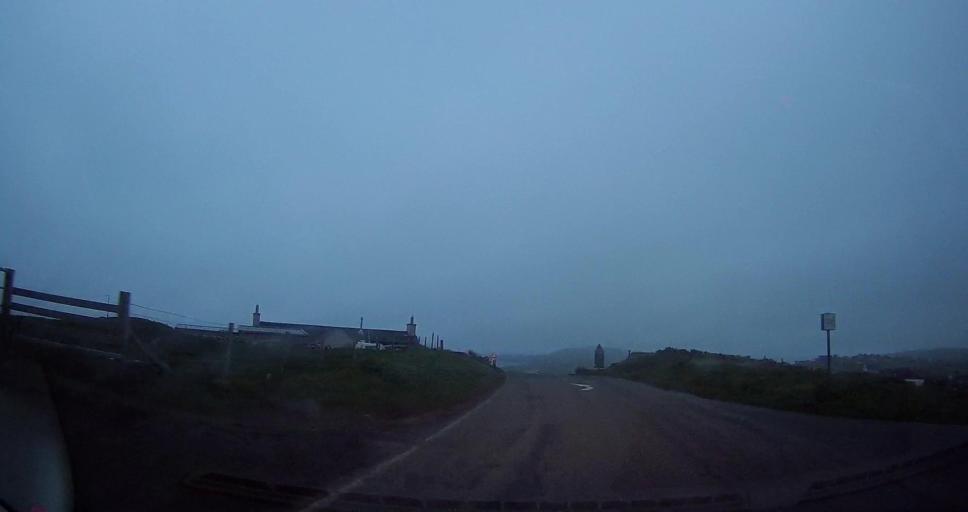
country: GB
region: Scotland
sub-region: Shetland Islands
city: Sandwick
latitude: 60.0142
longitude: -1.2274
